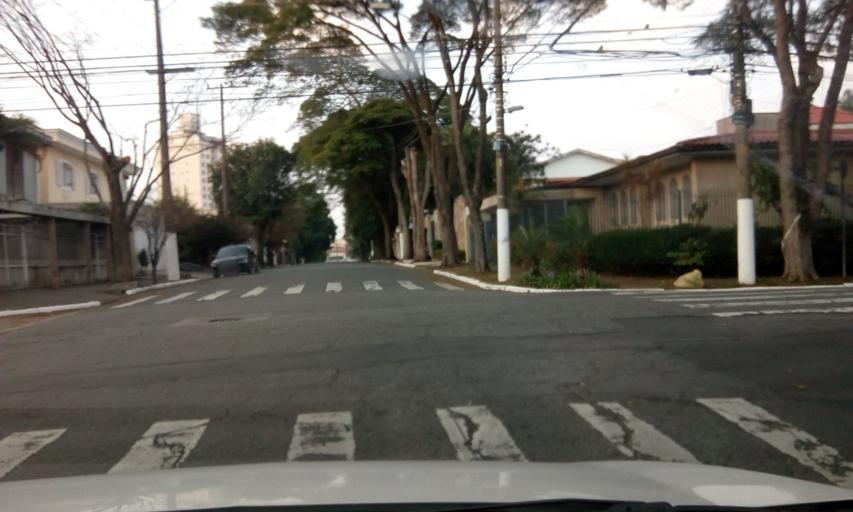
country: BR
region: Sao Paulo
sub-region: Diadema
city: Diadema
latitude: -23.6197
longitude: -46.6521
